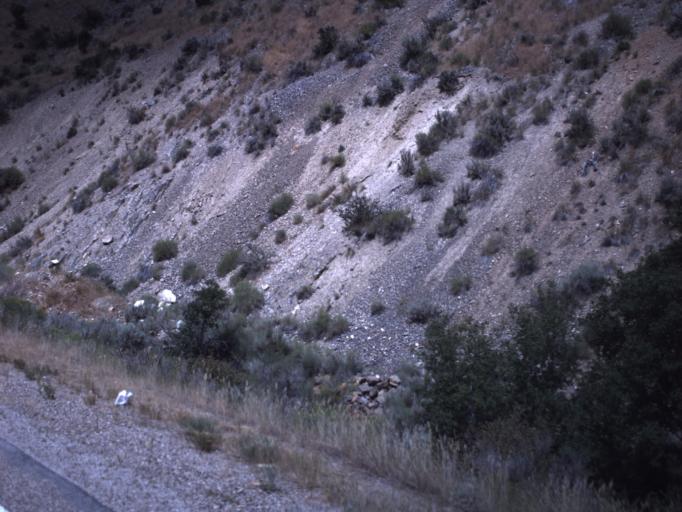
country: US
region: Utah
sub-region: Rich County
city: Randolph
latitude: 41.8244
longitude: -111.2989
